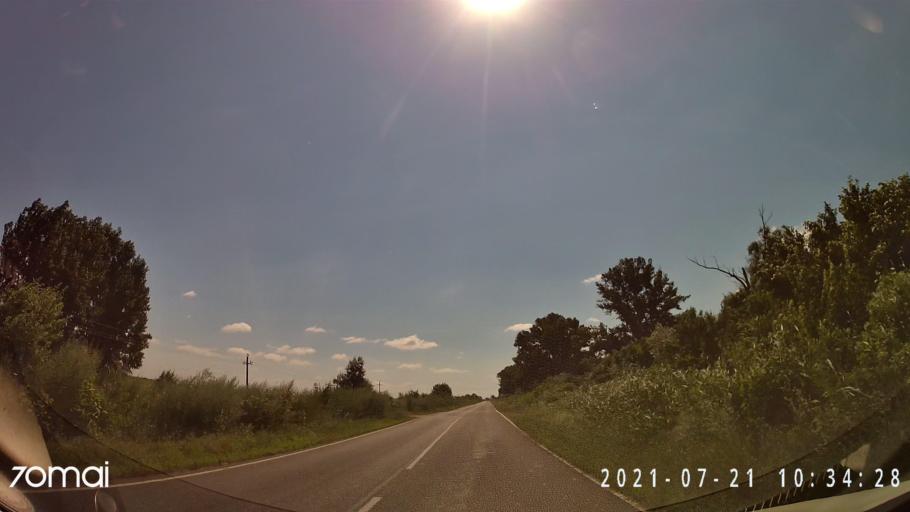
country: RO
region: Tulcea
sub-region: Oras Isaccea
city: Isaccea
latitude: 45.2952
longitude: 28.4475
